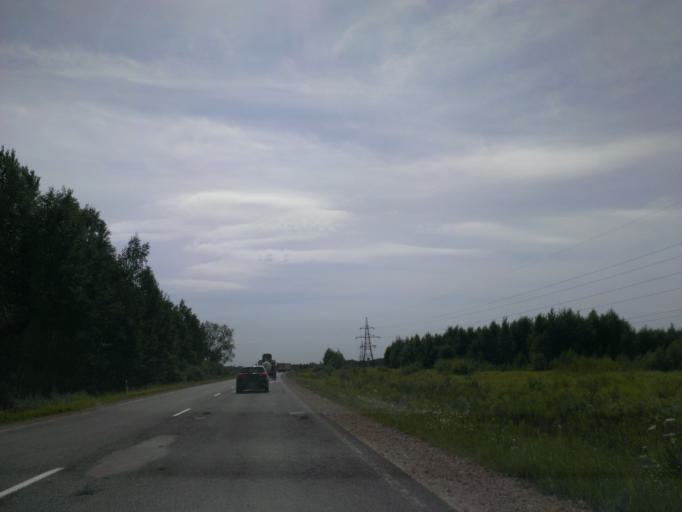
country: LV
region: Salaspils
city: Salaspils
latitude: 56.8662
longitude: 24.4066
